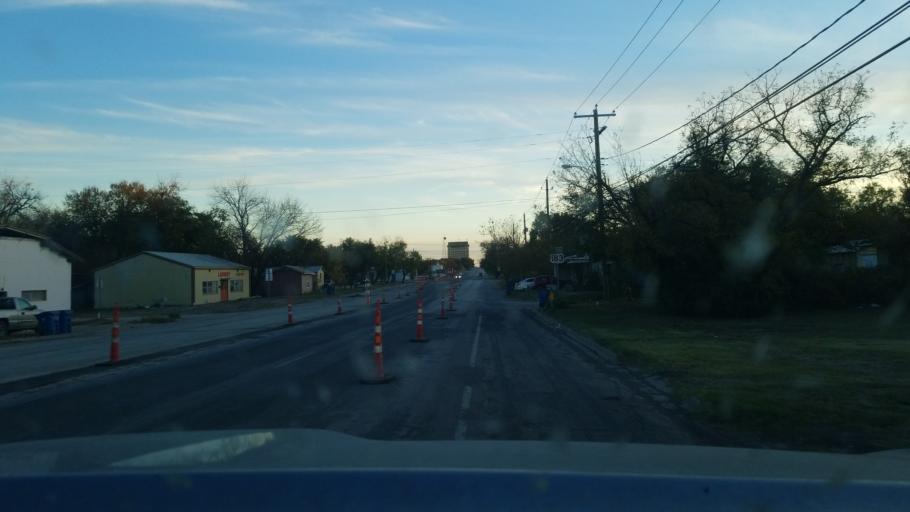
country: US
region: Texas
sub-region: Stephens County
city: Breckenridge
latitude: 32.7645
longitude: -98.9028
